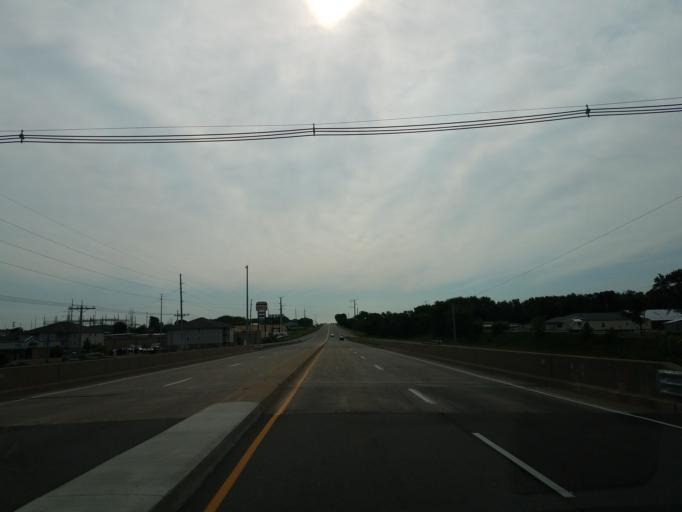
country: US
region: Illinois
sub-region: McLean County
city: Bloomington
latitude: 40.4591
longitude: -88.9933
